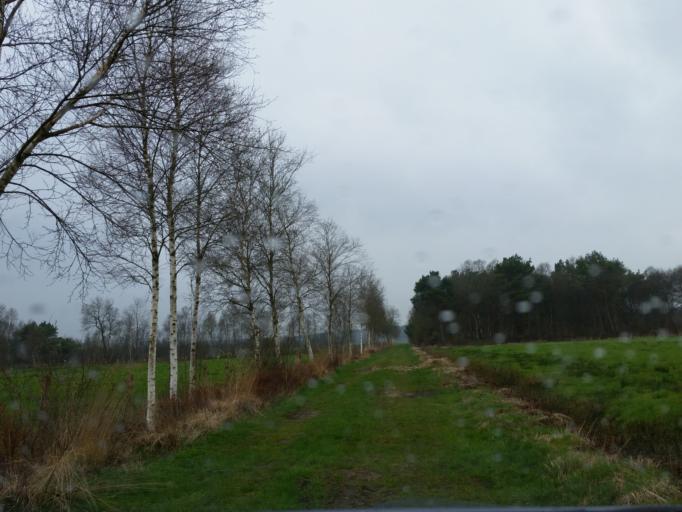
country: DE
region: Lower Saxony
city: Stinstedt
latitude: 53.6012
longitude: 8.9807
